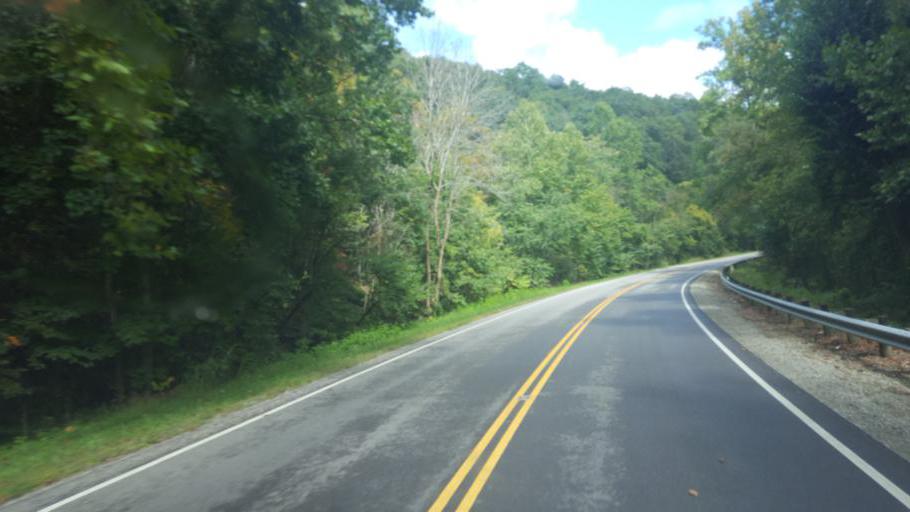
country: US
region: Ohio
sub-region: Scioto County
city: Sciotodale
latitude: 38.8863
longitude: -82.7865
